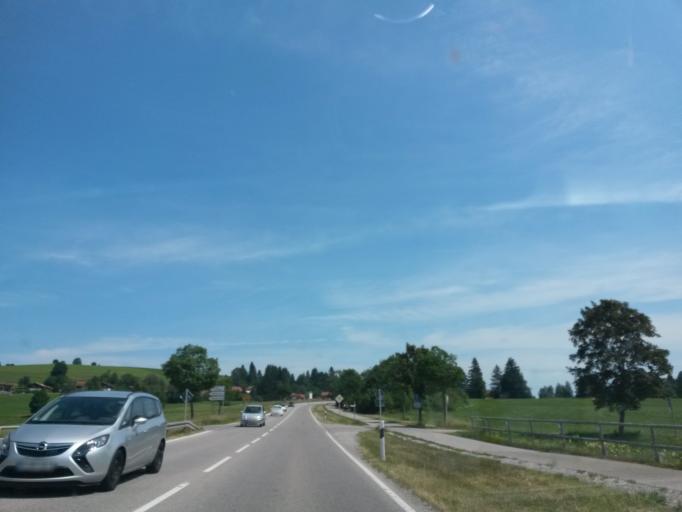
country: DE
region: Bavaria
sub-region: Swabia
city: Halblech
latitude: 47.6457
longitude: 10.8288
